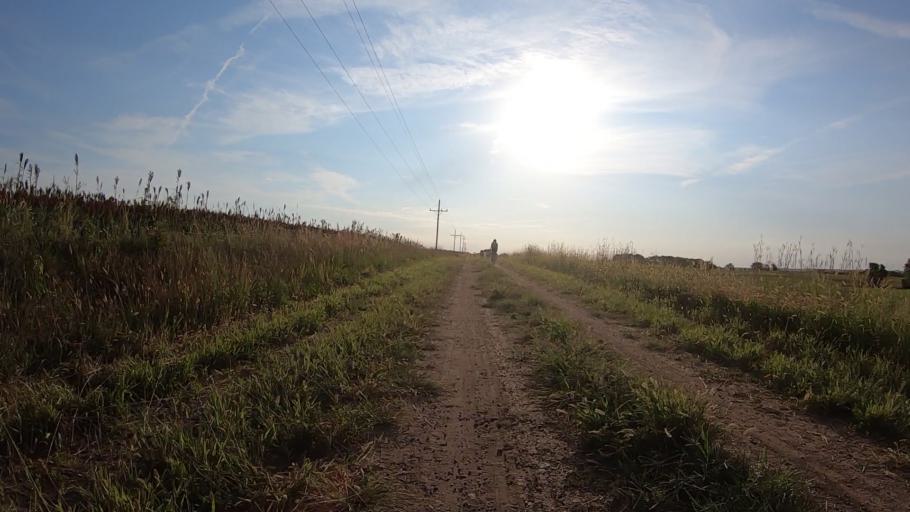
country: US
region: Kansas
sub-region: Marshall County
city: Blue Rapids
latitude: 39.7114
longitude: -96.8042
